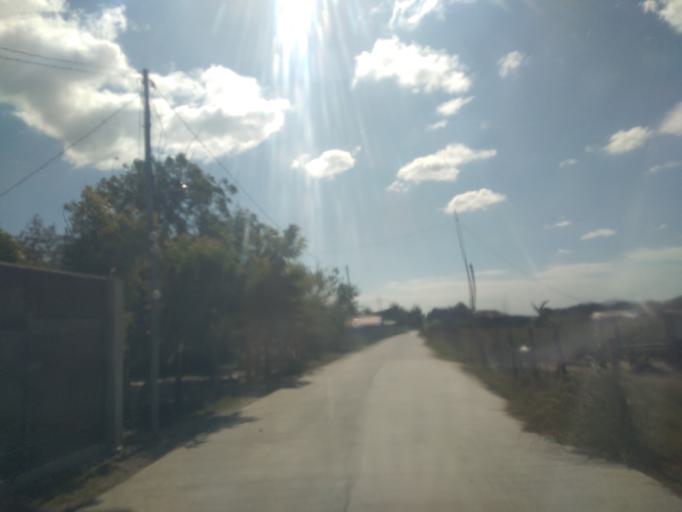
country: PH
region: Central Luzon
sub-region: Province of Pampanga
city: Balas
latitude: 15.0777
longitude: 120.6016
